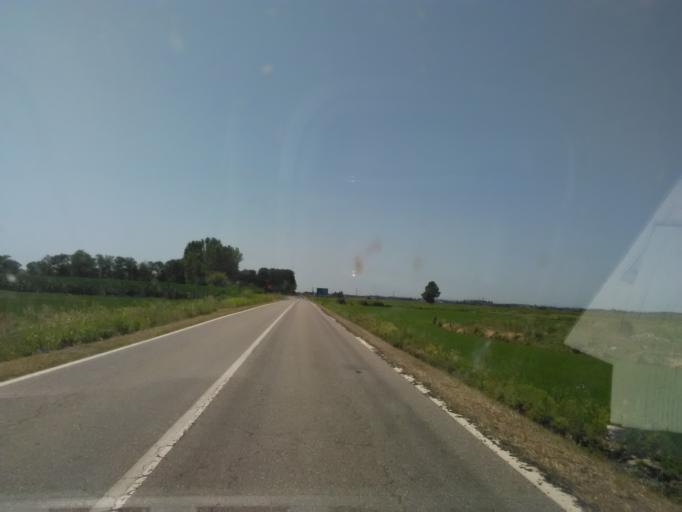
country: IT
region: Piedmont
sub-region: Provincia di Vercelli
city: Arborio
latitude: 45.4787
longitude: 8.3877
